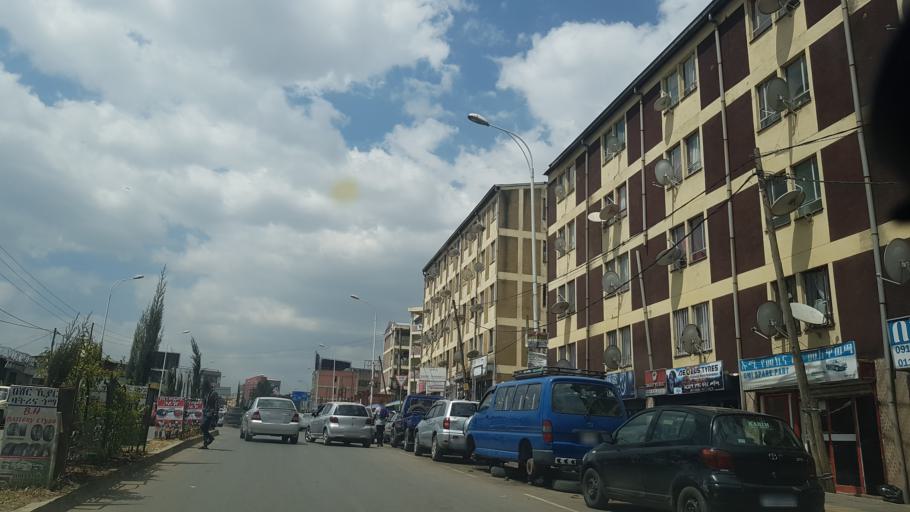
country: ET
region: Adis Abeba
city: Addis Ababa
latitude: 9.0284
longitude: 38.7461
